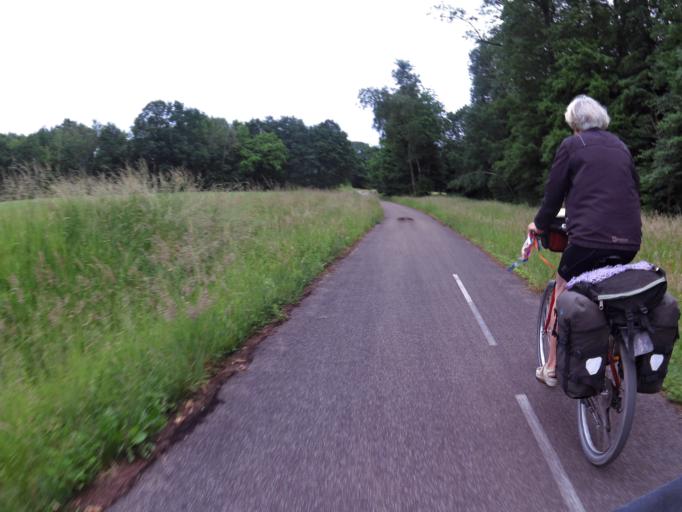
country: FR
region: Champagne-Ardenne
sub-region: Departement de la Haute-Marne
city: Montier-en-Der
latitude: 48.5452
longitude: 4.8086
